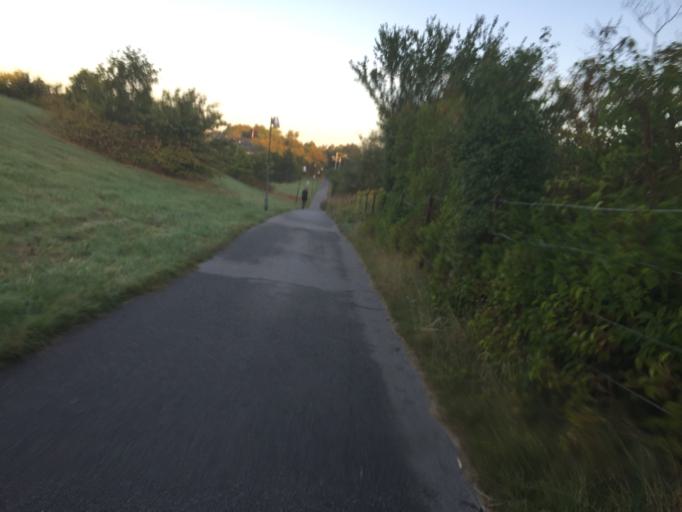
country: DK
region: Capital Region
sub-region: Ballerup Kommune
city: Malov
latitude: 55.7486
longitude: 12.3153
